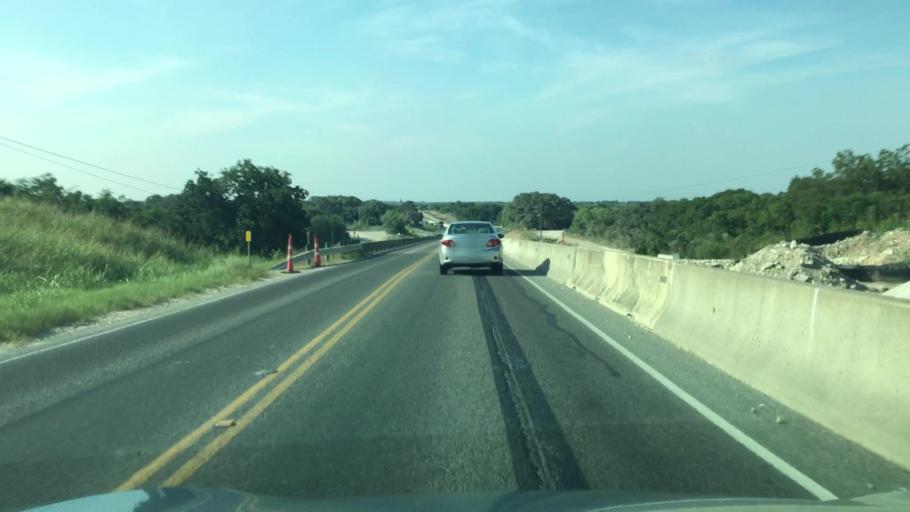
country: US
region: Texas
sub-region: Hays County
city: Buda
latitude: 30.0573
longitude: -97.8741
